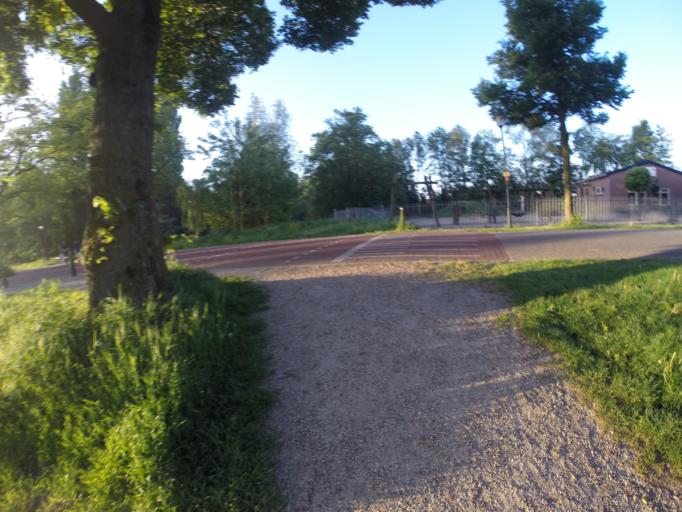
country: NL
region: Gelderland
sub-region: Gemeente Doetinchem
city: Doetinchem
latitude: 51.9563
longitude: 6.2796
